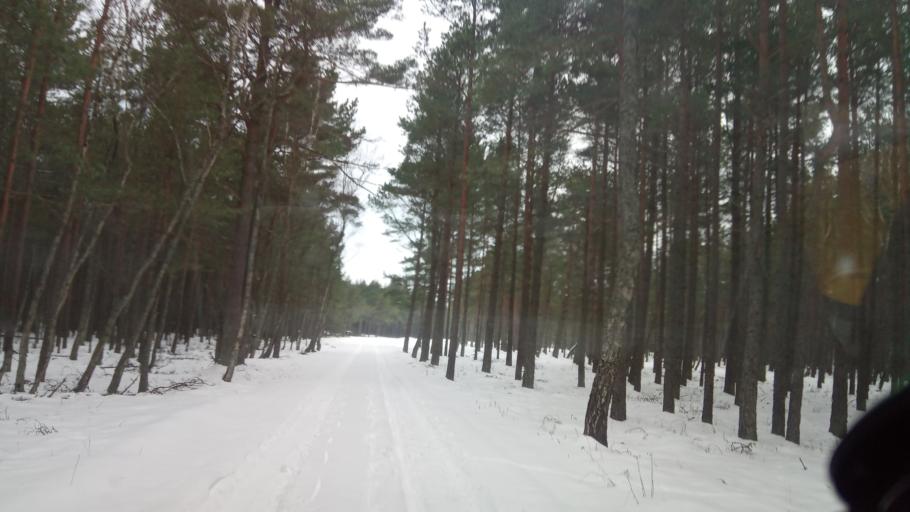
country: LT
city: Neringa
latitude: 55.4228
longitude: 21.0943
